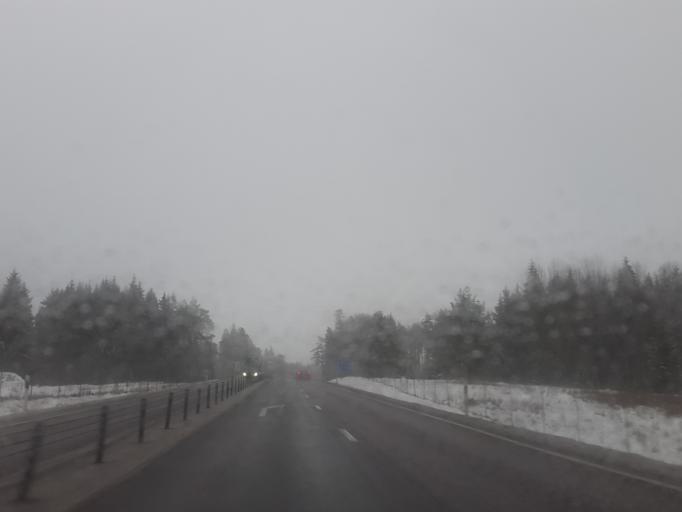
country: SE
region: Joenkoeping
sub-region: Jonkopings Kommun
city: Taberg
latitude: 57.7601
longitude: 14.0055
